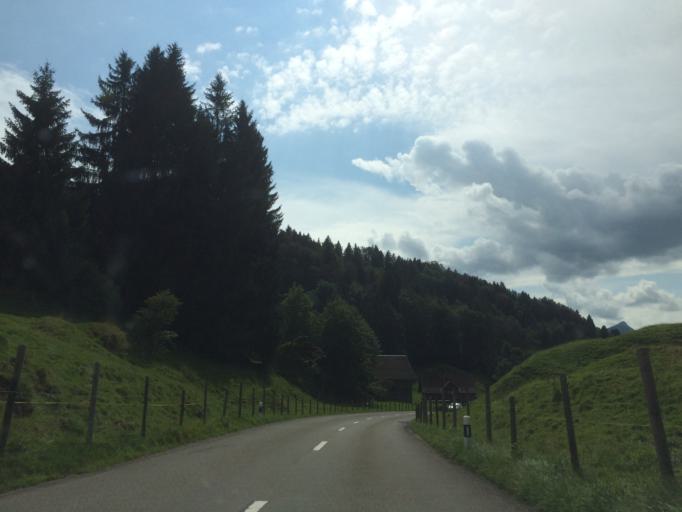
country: CH
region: Saint Gallen
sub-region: Wahlkreis Toggenburg
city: Krummenau
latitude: 47.2427
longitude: 9.2269
